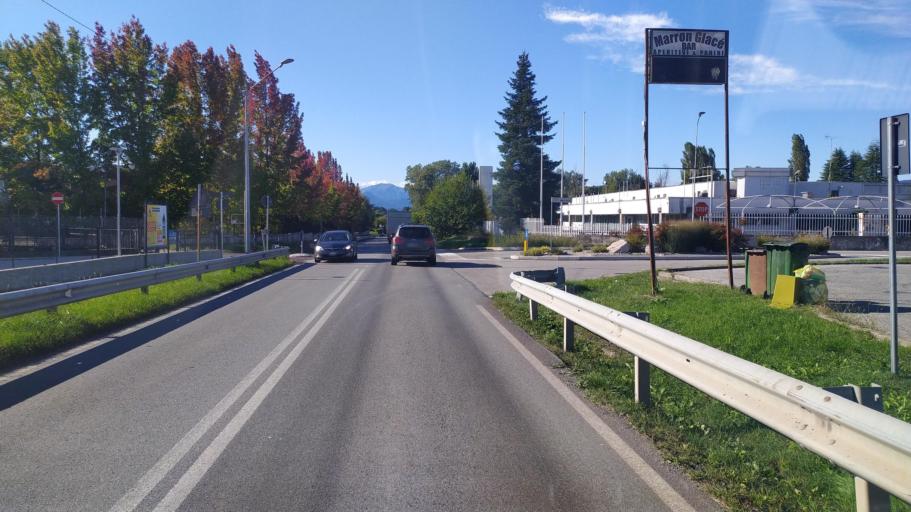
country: IT
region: Lombardy
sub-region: Provincia di Varese
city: Bodio Lomnago
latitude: 45.7915
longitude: 8.7452
